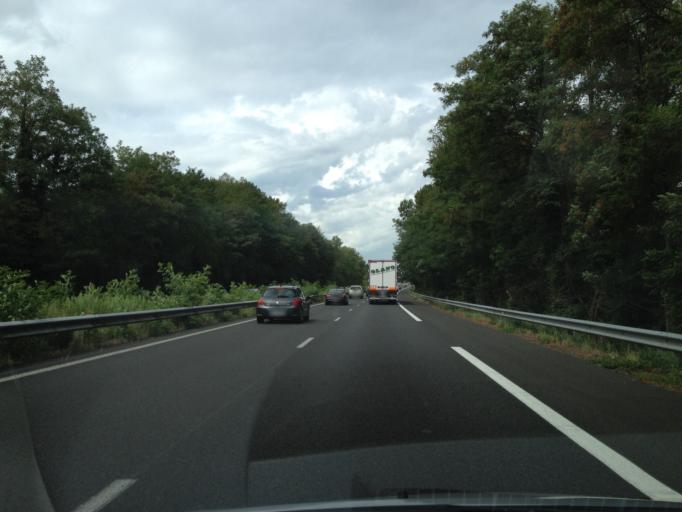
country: FR
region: Aquitaine
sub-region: Departement de la Gironde
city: Castets-en-Dorthe
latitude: 44.5303
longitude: -0.1578
